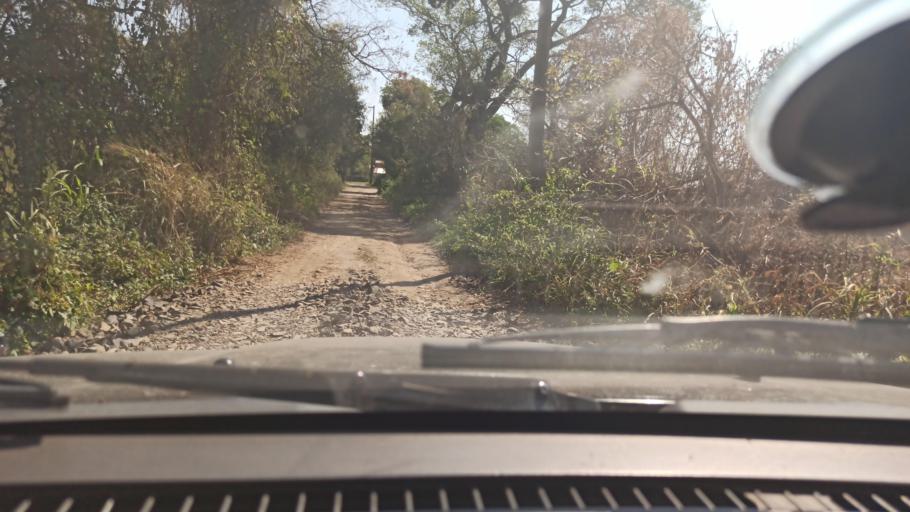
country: PY
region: Asuncion
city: Asuncion
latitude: -25.3333
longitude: -57.6817
